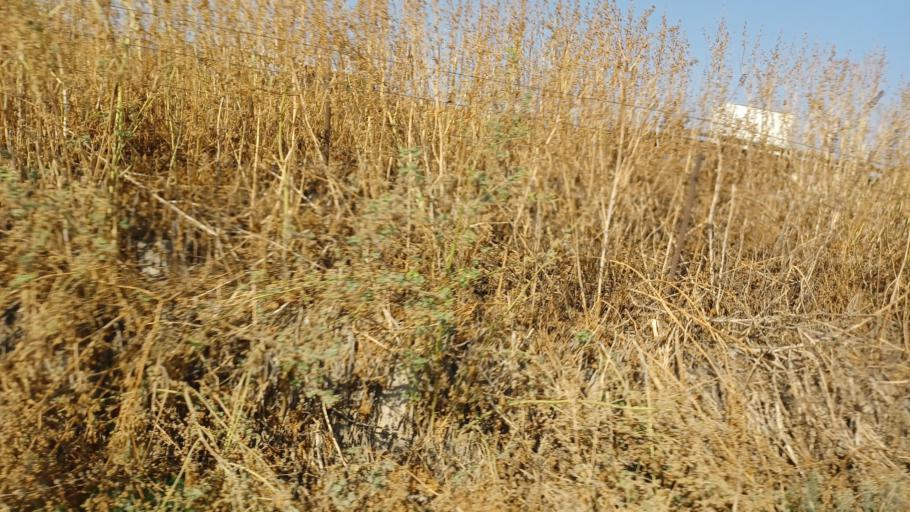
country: CY
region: Lefkosia
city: Lympia
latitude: 34.9882
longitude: 33.4719
